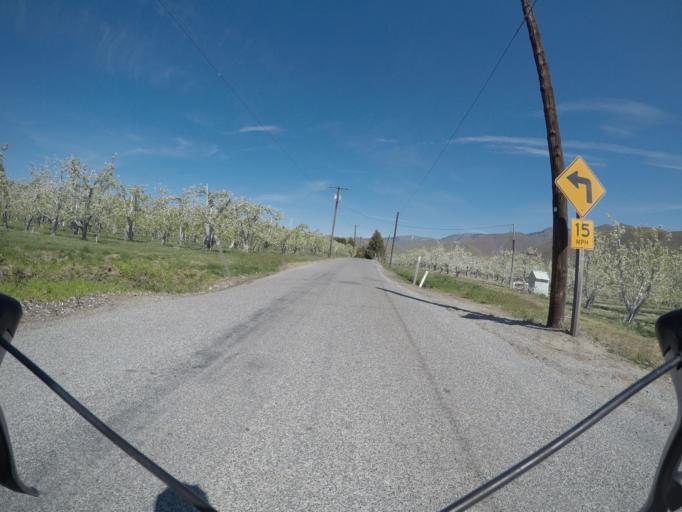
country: US
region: Washington
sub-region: Chelan County
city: Cashmere
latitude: 47.4916
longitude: -120.4316
